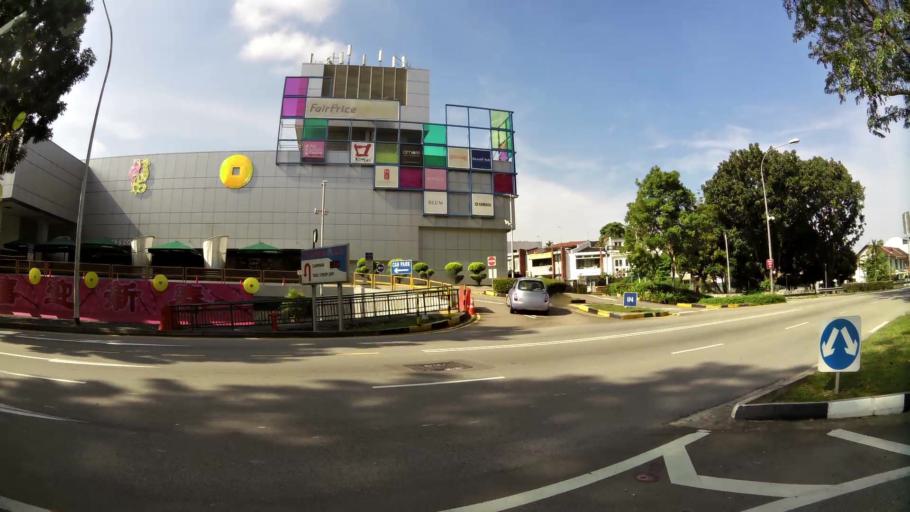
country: SG
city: Singapore
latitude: 1.3555
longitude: 103.8308
